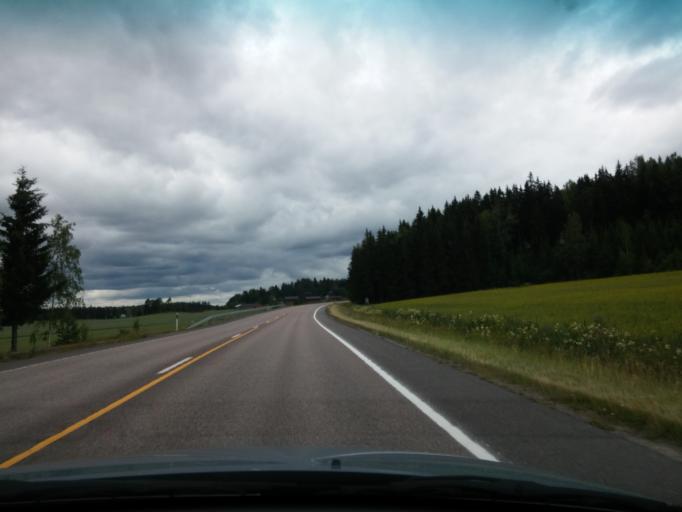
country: FI
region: Uusimaa
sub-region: Porvoo
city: Askola
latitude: 60.4855
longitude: 25.5596
